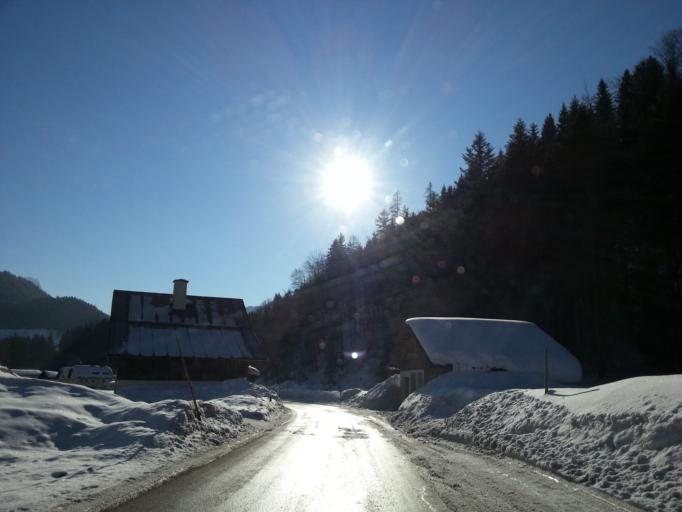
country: AT
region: Salzburg
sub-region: Politischer Bezirk Hallein
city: Abtenau
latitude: 47.4947
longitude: 13.3939
